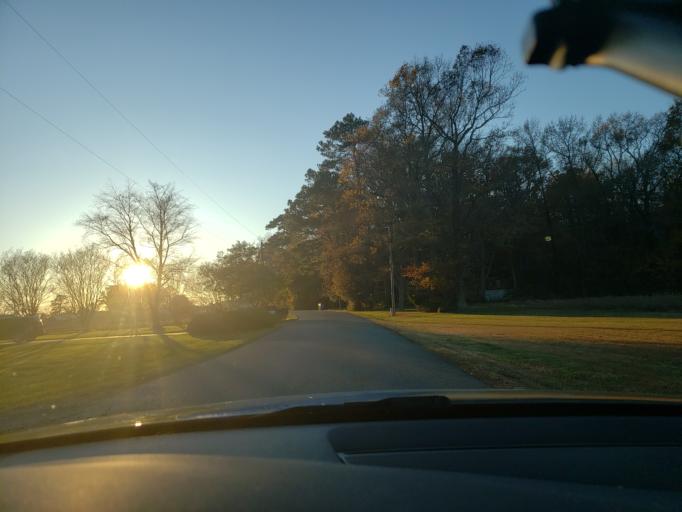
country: US
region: Virginia
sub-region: City of Chesapeake
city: Chesapeake
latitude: 36.7046
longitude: -76.1569
